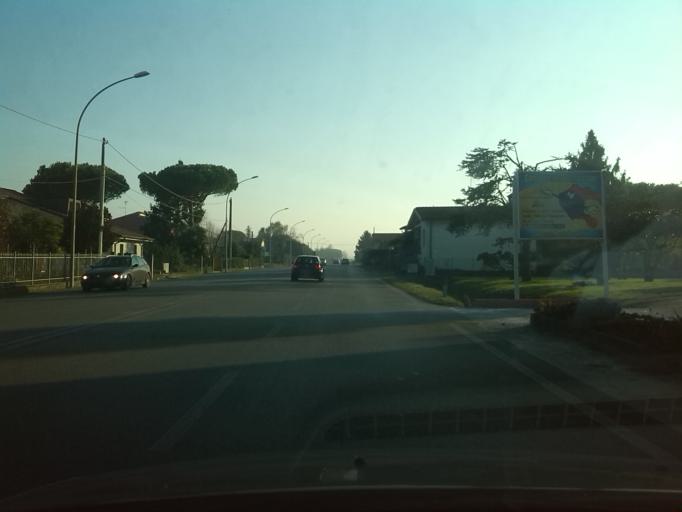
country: IT
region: Friuli Venezia Giulia
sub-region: Provincia di Udine
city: Pertegada
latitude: 45.7176
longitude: 13.0503
